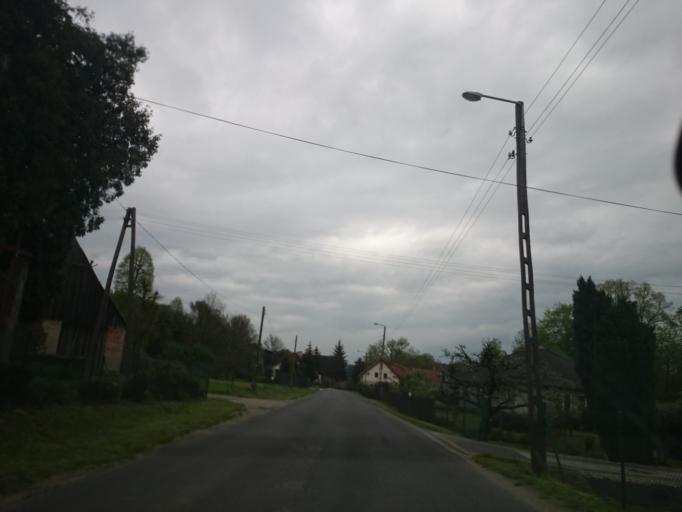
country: PL
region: Lower Silesian Voivodeship
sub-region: Powiat klodzki
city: Klodzko
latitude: 50.4148
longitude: 16.6947
